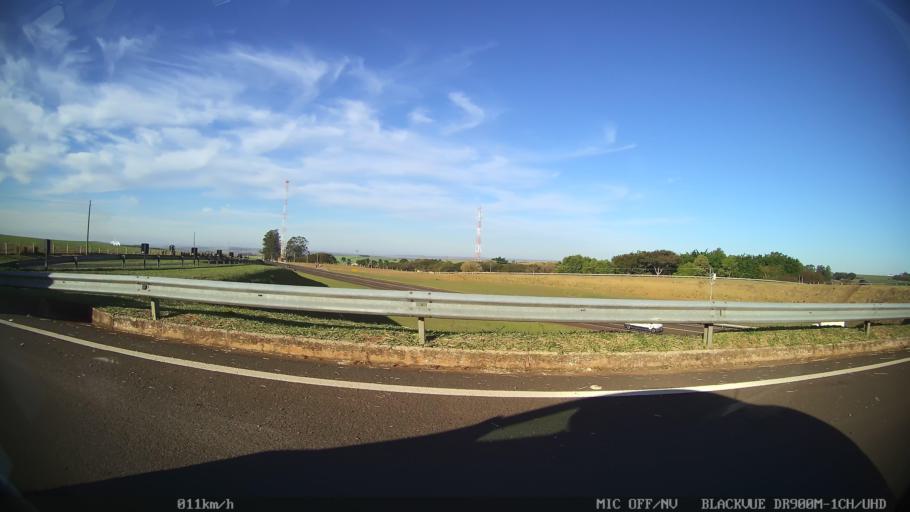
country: BR
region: Sao Paulo
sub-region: Americo Brasiliense
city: Americo Brasiliense
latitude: -21.7745
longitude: -48.1016
